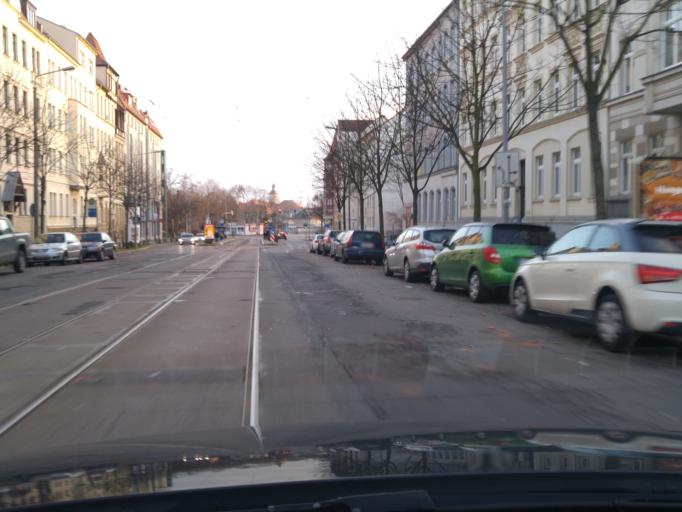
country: DE
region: Saxony
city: Leipzig
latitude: 51.3689
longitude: 12.3658
